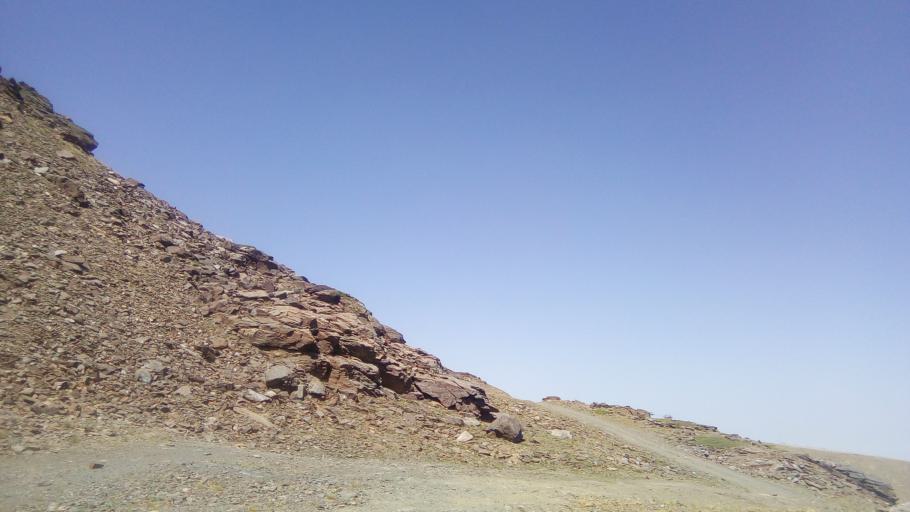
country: ES
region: Andalusia
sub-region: Provincia de Granada
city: Guejar-Sierra
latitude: 37.0714
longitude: -3.3927
